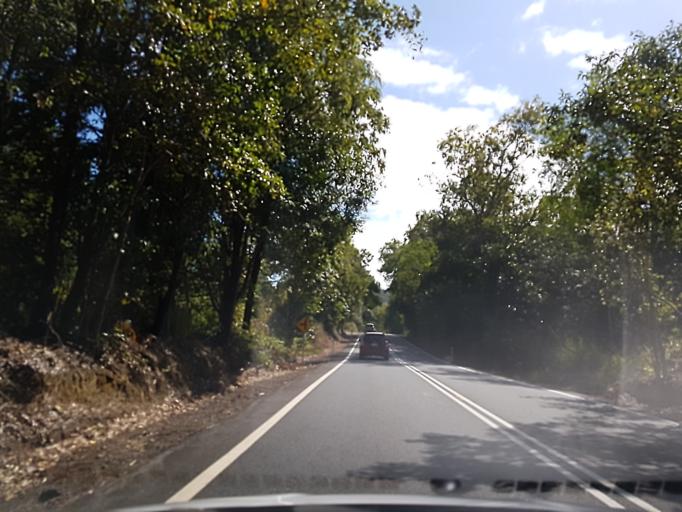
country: AU
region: Queensland
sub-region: Cairns
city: Port Douglas
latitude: -16.5856
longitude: 145.5133
